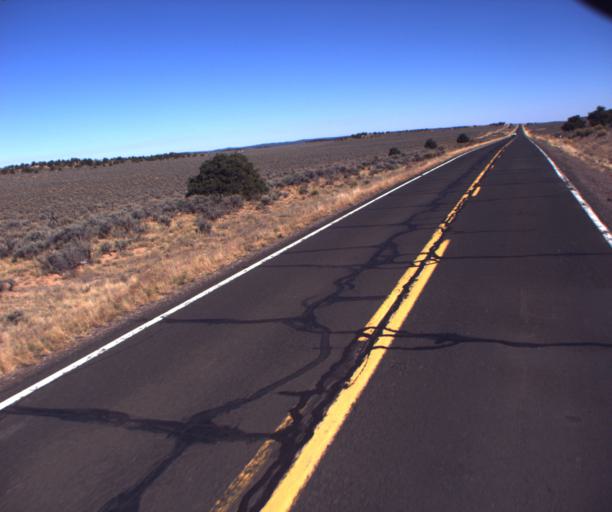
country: US
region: Arizona
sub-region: Navajo County
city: First Mesa
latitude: 35.7457
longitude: -110.0578
